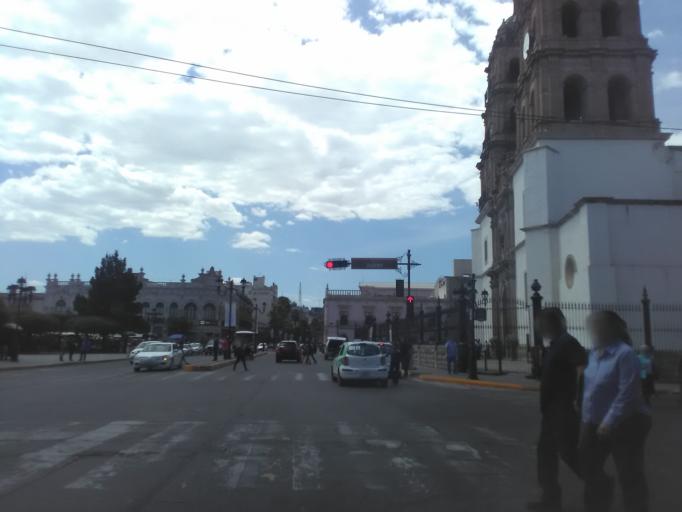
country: MX
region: Durango
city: Victoria de Durango
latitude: 24.0248
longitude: -104.6698
